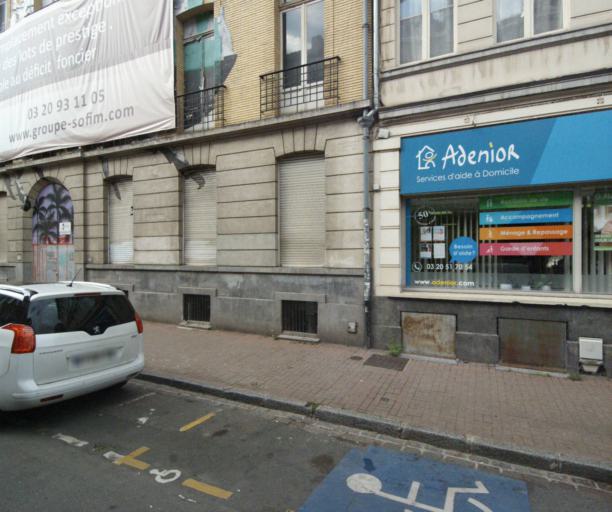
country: FR
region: Nord-Pas-de-Calais
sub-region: Departement du Nord
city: Lille
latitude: 50.6302
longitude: 3.0613
